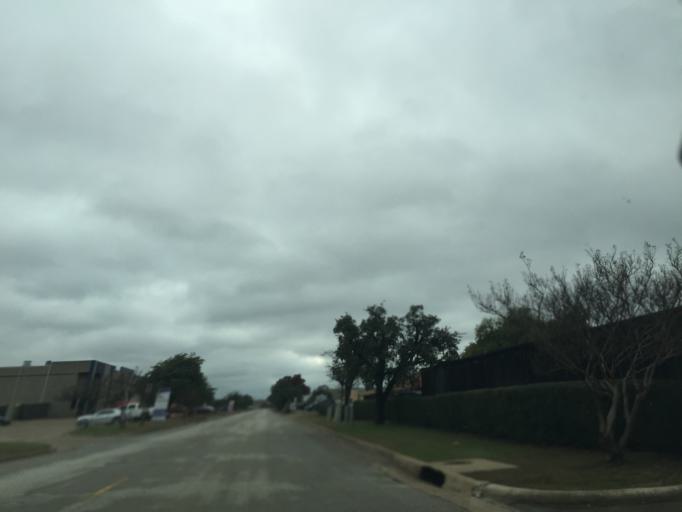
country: US
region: Texas
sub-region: Tarrant County
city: Arlington
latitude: 32.7539
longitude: -97.0574
